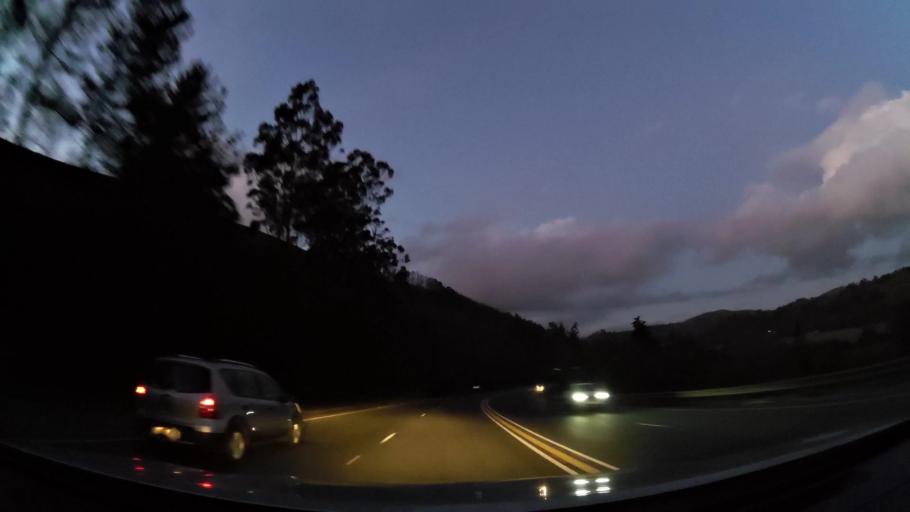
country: ZA
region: Western Cape
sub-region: Eden District Municipality
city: Knysna
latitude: -34.0375
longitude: 22.9266
